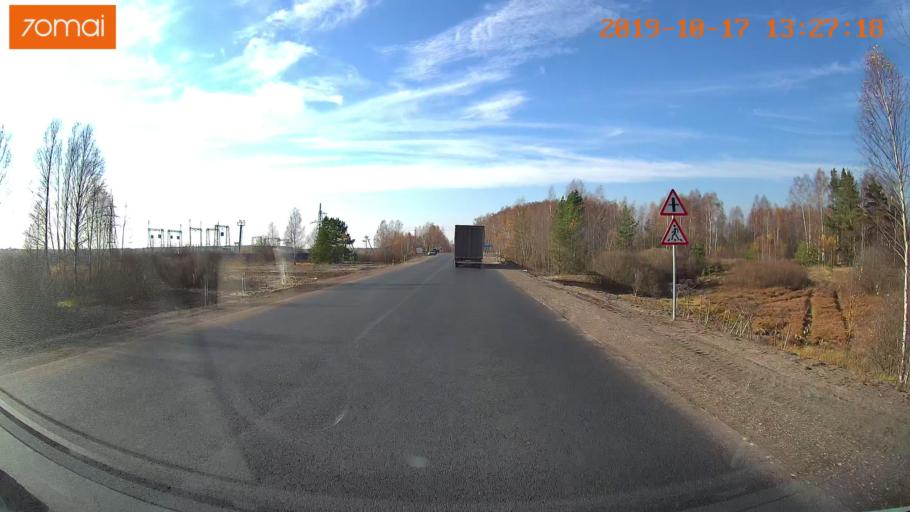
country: RU
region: Vladimir
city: Velikodvorskiy
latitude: 55.1128
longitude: 40.8986
